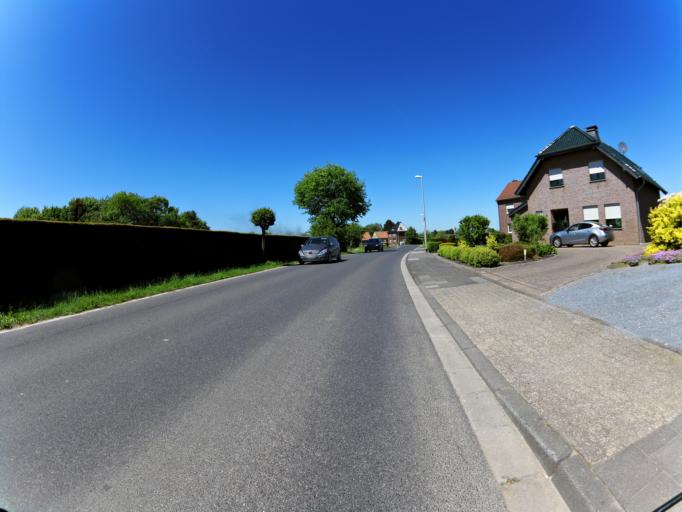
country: DE
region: North Rhine-Westphalia
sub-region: Regierungsbezirk Koln
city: Gangelt
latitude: 51.0130
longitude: 6.0431
